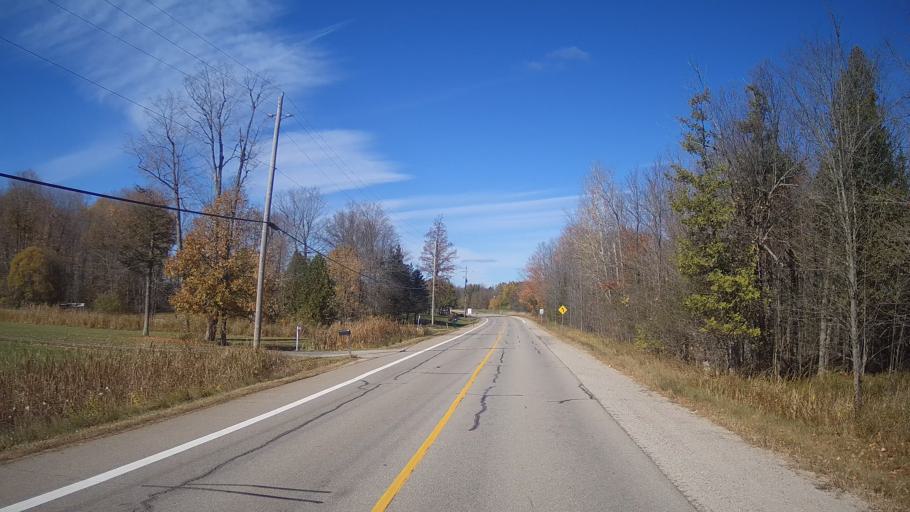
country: CA
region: Ontario
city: Perth
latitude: 44.8720
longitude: -76.2949
